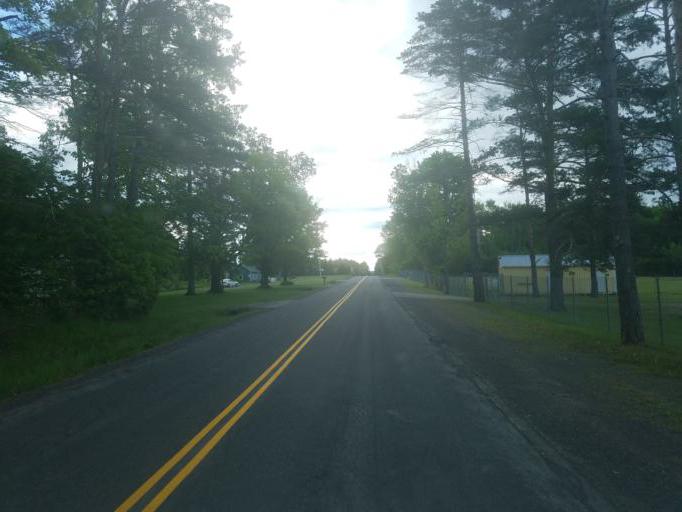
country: US
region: New York
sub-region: Herkimer County
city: Dolgeville
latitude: 43.3119
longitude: -74.9648
